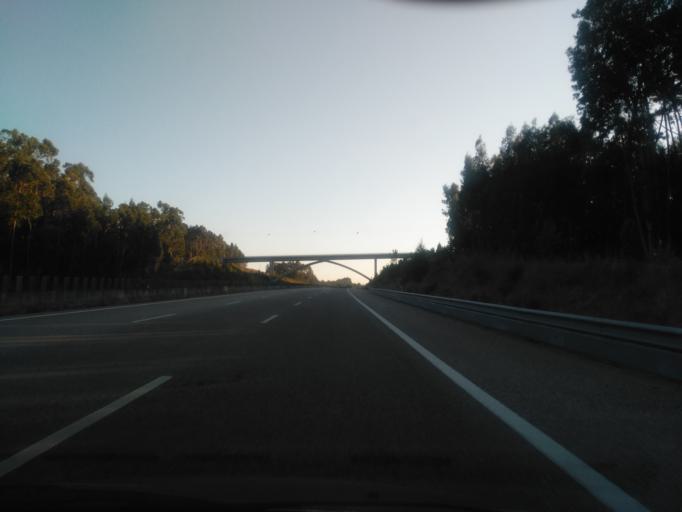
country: PT
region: Coimbra
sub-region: Figueira da Foz
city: Lavos
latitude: 40.0821
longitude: -8.7694
